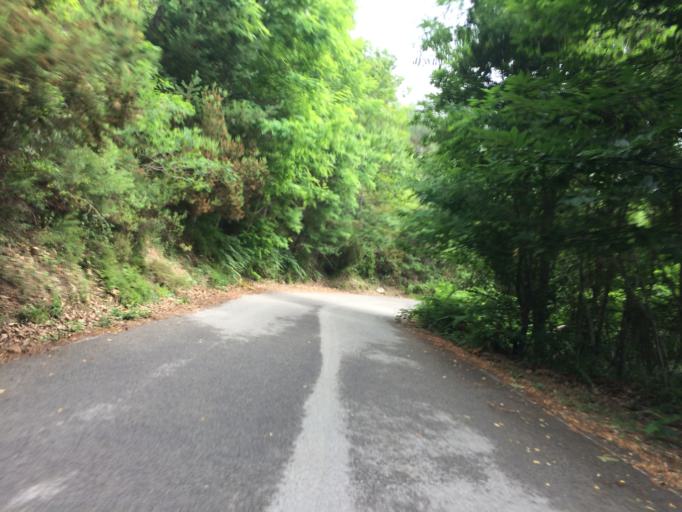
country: IT
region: Liguria
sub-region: Provincia di Imperia
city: Ceriana
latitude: 43.8605
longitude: 7.7413
